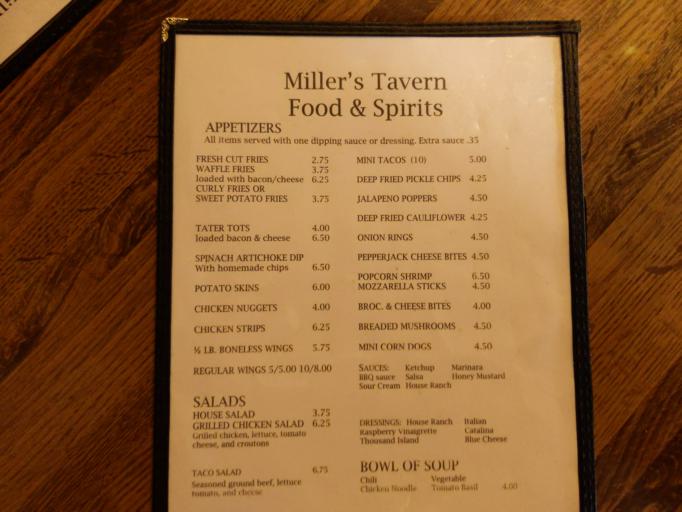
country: US
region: Michigan
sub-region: Clinton County
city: Fowler
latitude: 43.0023
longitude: -84.7395
